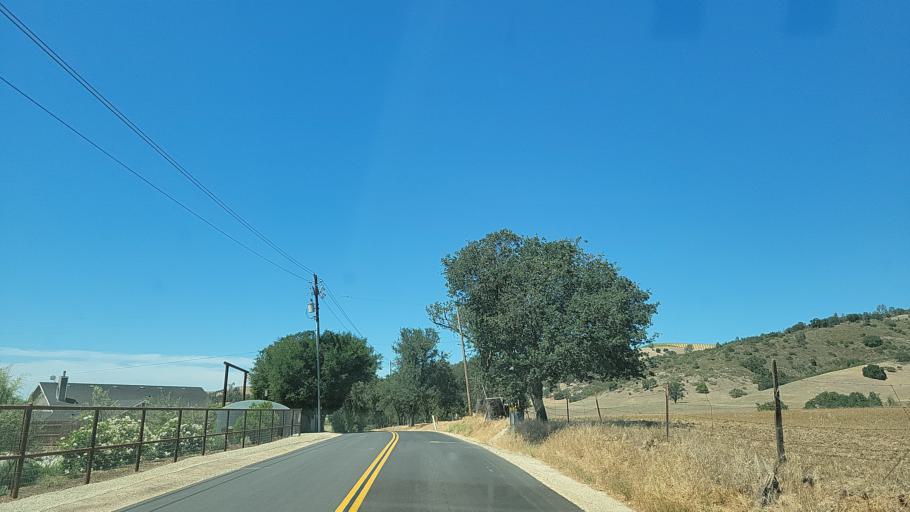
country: US
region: California
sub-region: San Luis Obispo County
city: Atascadero
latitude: 35.4667
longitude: -120.6235
